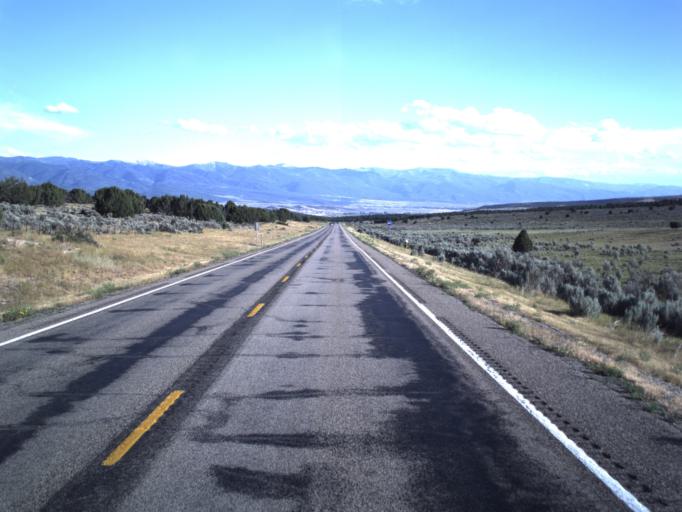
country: US
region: Utah
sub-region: Sanpete County
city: Fairview
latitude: 39.6863
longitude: -111.4591
